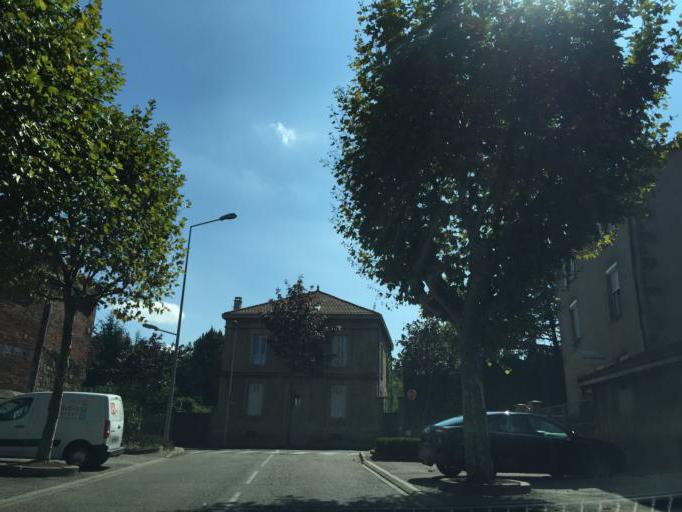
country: FR
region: Rhone-Alpes
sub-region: Departement de la Loire
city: Saint-Chamond
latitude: 45.4670
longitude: 4.5183
